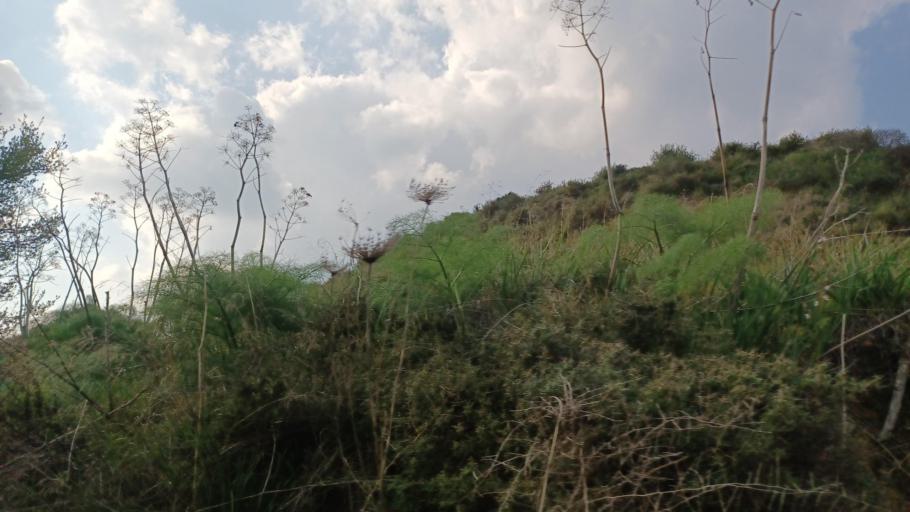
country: CY
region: Pafos
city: Polis
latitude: 35.0352
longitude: 32.4647
